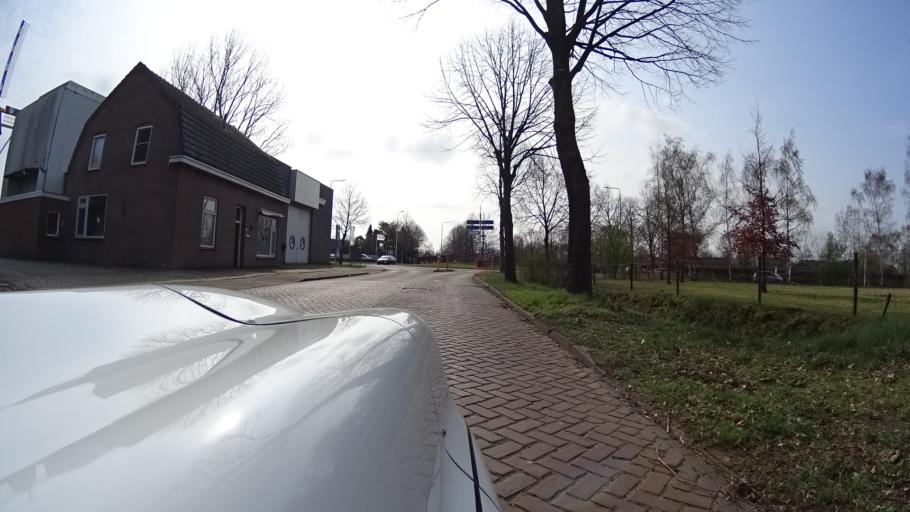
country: NL
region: North Brabant
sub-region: Gemeente Boekel
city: Boekel
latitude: 51.5466
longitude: 5.6892
